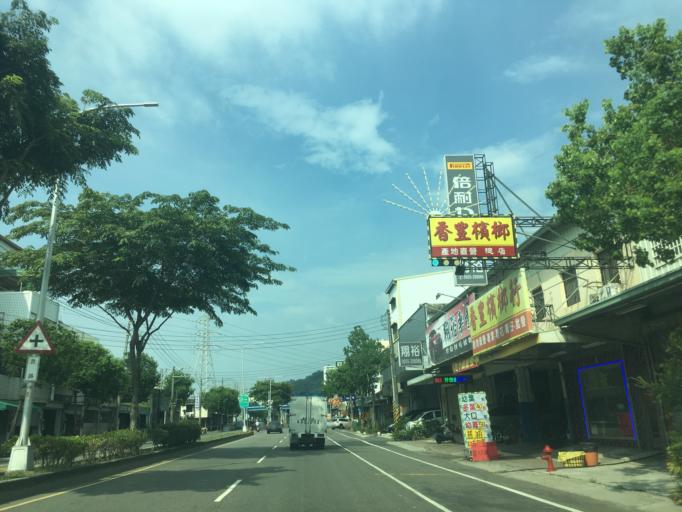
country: TW
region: Taiwan
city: Fengyuan
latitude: 24.2628
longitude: 120.7407
